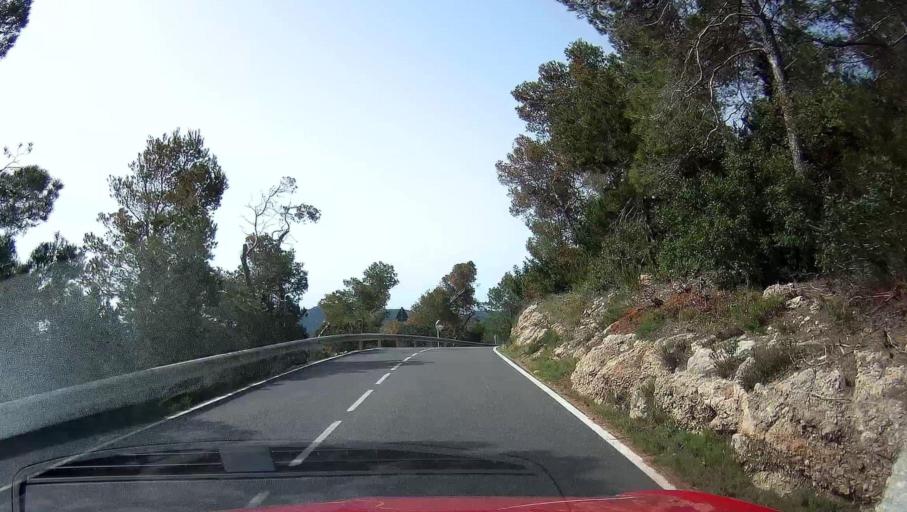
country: ES
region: Balearic Islands
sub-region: Illes Balears
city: Sant Joan de Labritja
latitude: 39.0662
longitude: 1.5879
